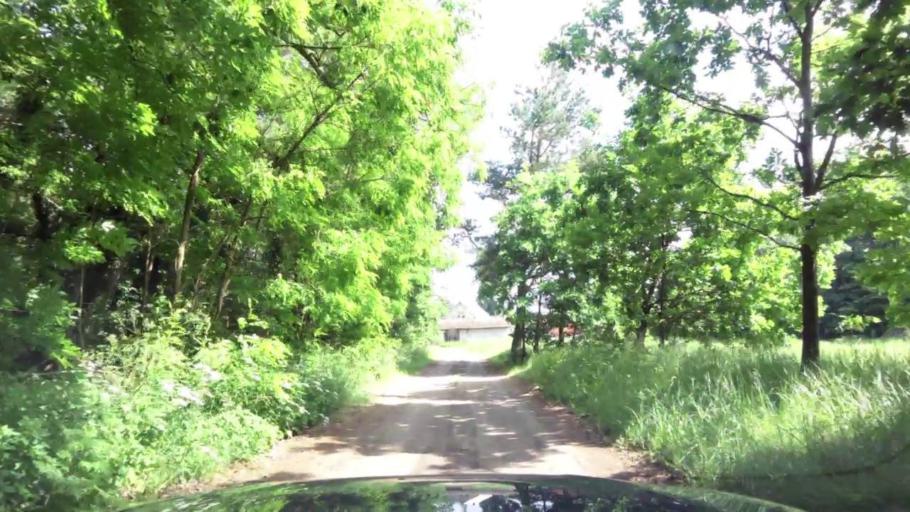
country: PL
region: West Pomeranian Voivodeship
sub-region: Powiat pyrzycki
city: Lipiany
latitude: 52.9637
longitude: 14.9229
